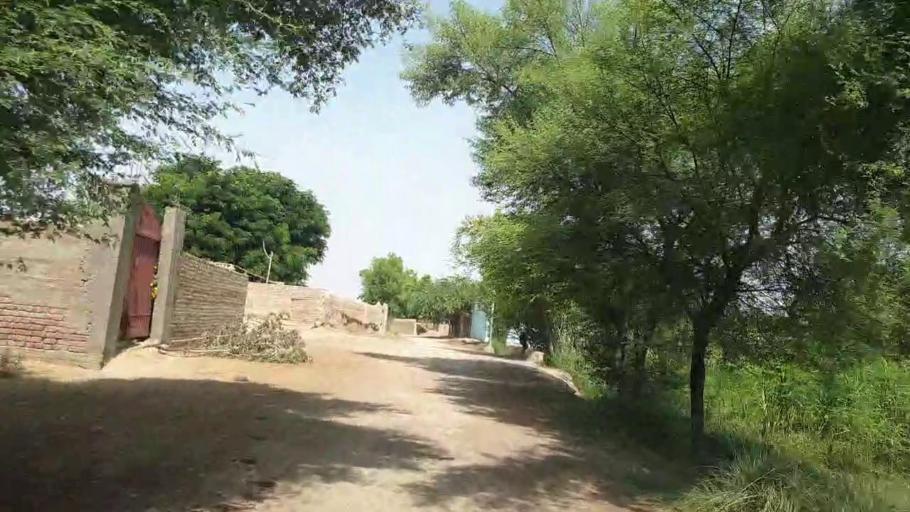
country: PK
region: Sindh
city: Bozdar
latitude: 27.0877
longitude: 68.6041
